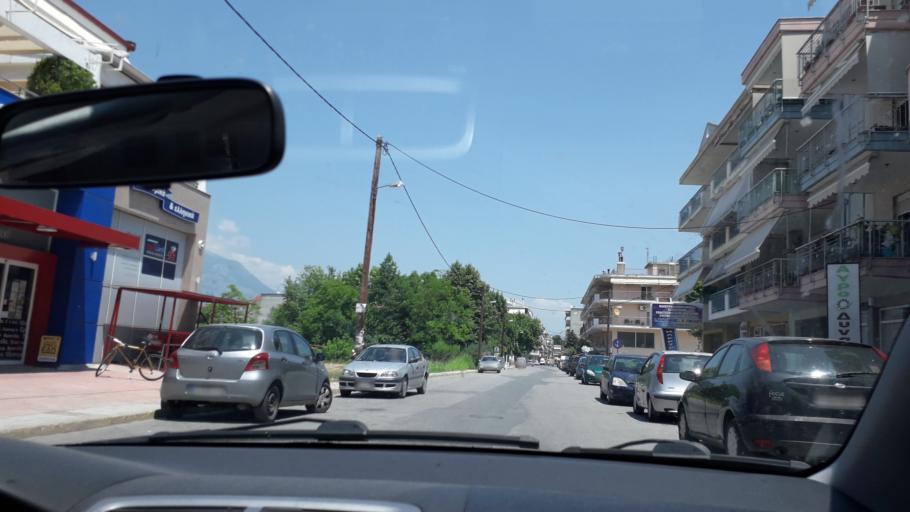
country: GR
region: Central Macedonia
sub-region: Nomos Pellis
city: Aridaia
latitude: 40.9715
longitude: 22.0585
